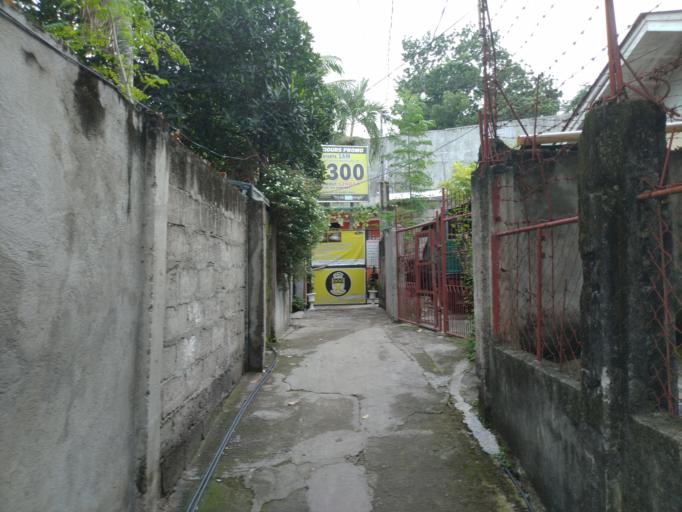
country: PH
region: Central Visayas
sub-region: Province of Negros Oriental
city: Dumaguete
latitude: 9.3045
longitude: 123.2995
